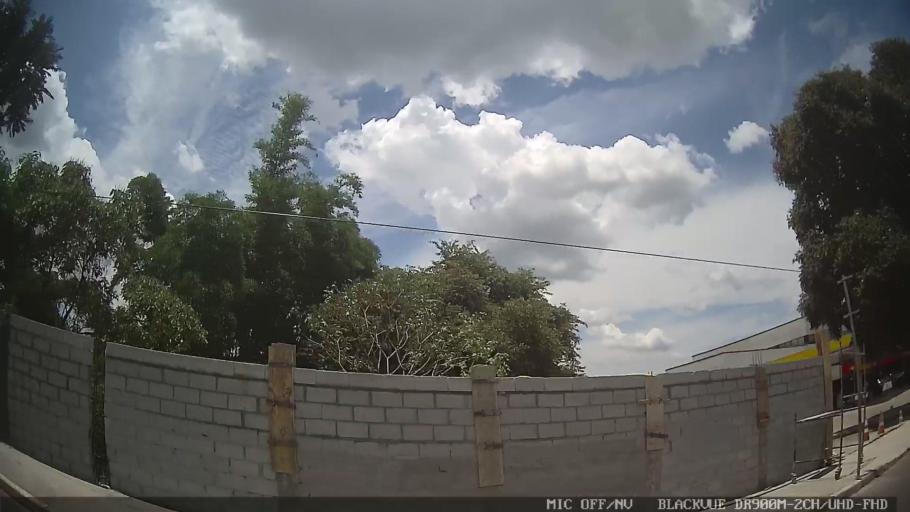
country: BR
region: Sao Paulo
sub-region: Atibaia
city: Atibaia
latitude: -23.1165
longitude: -46.5774
